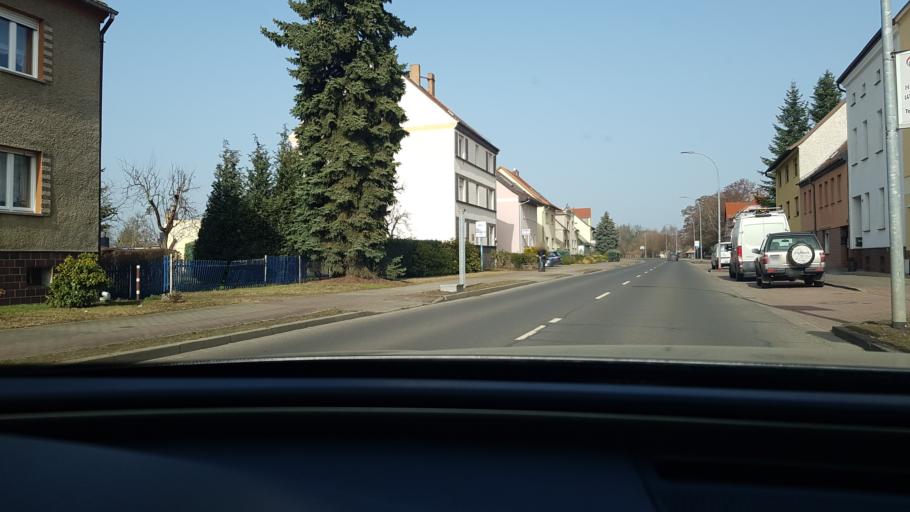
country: DE
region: Brandenburg
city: Guben
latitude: 51.9625
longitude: 14.7023
